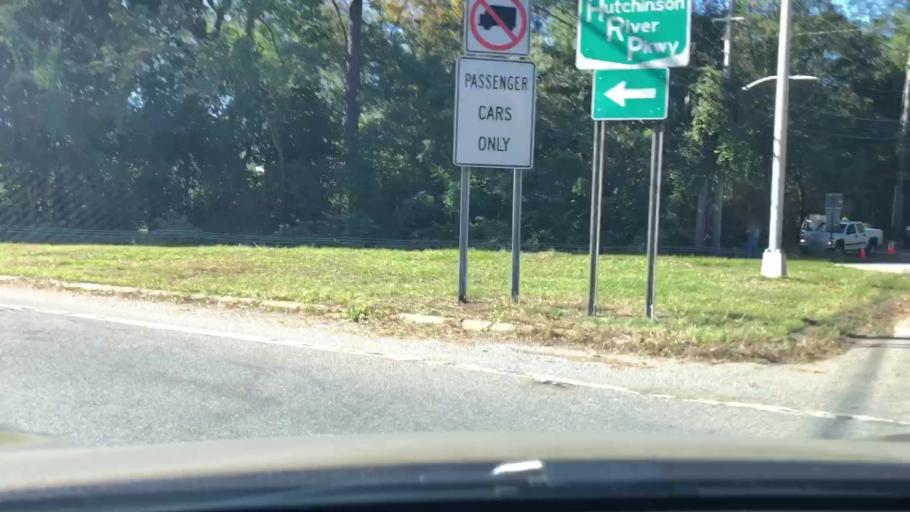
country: US
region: New York
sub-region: Westchester County
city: Harrison
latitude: 41.0004
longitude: -73.7266
